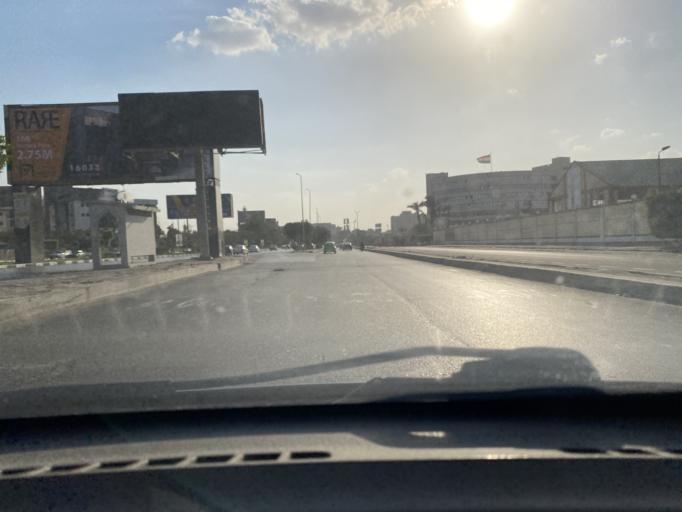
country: EG
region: Muhafazat al Qahirah
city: Cairo
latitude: 30.0729
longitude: 31.2986
